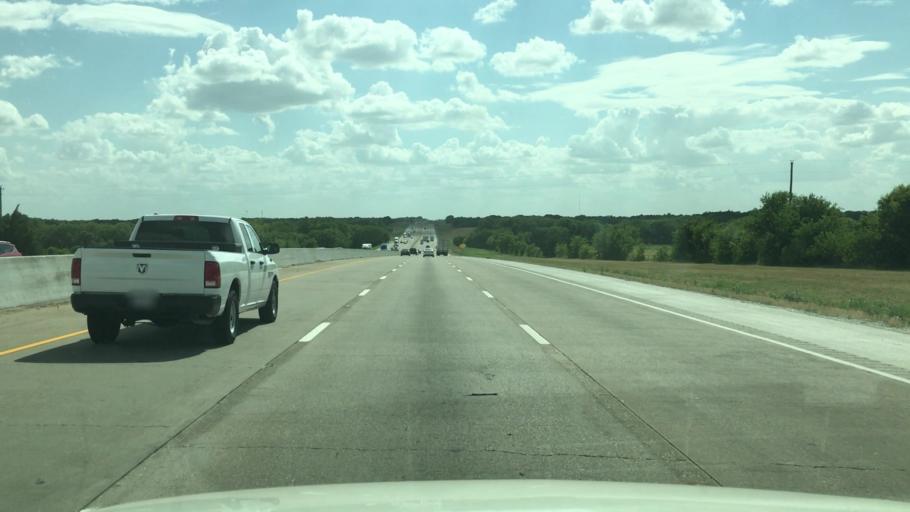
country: US
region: Texas
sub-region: Ellis County
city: Plum Grove
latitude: 32.1244
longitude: -96.9731
